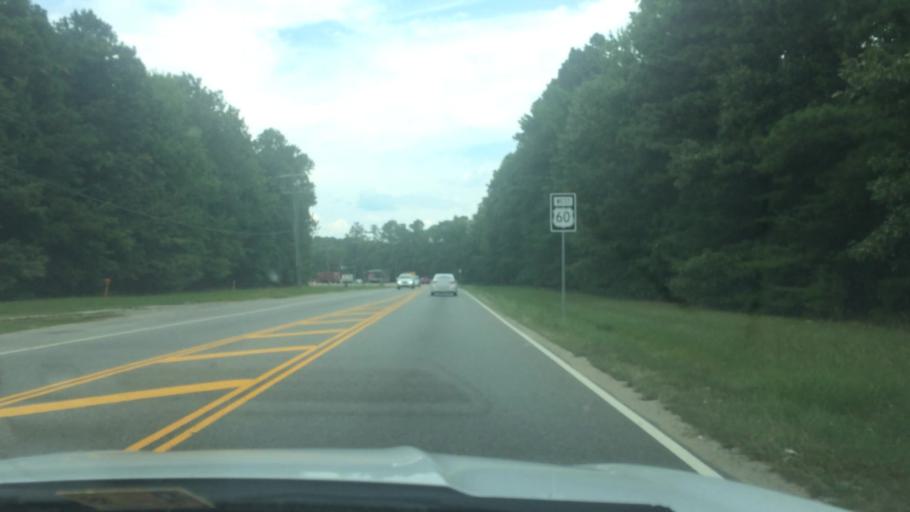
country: US
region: Virginia
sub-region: York County
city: Yorktown
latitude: 37.1781
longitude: -76.5698
